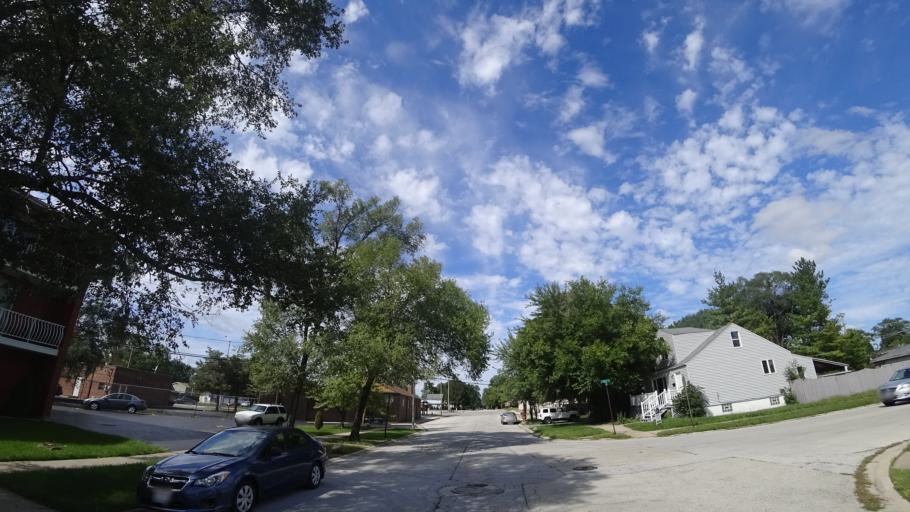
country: US
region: Illinois
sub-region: Cook County
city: Oak Lawn
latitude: 41.7159
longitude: -87.7712
